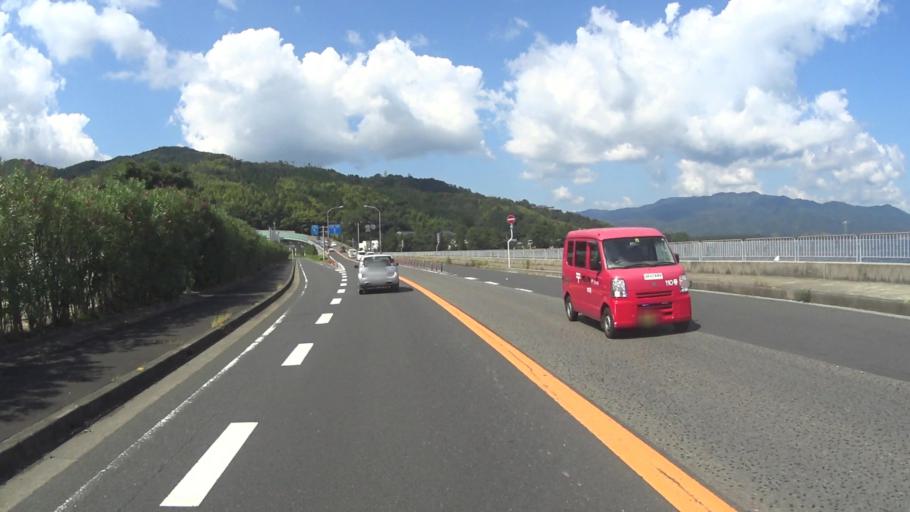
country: JP
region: Kyoto
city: Miyazu
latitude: 35.5455
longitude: 135.1898
